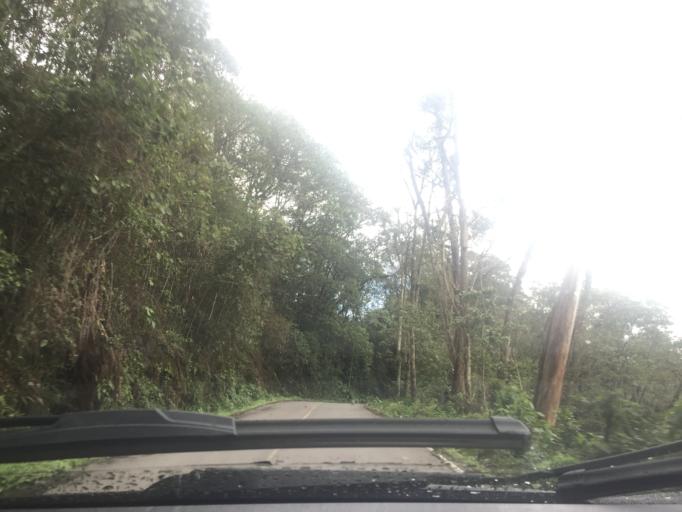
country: CO
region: Cundinamarca
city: Supata
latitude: 5.0333
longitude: -74.2566
